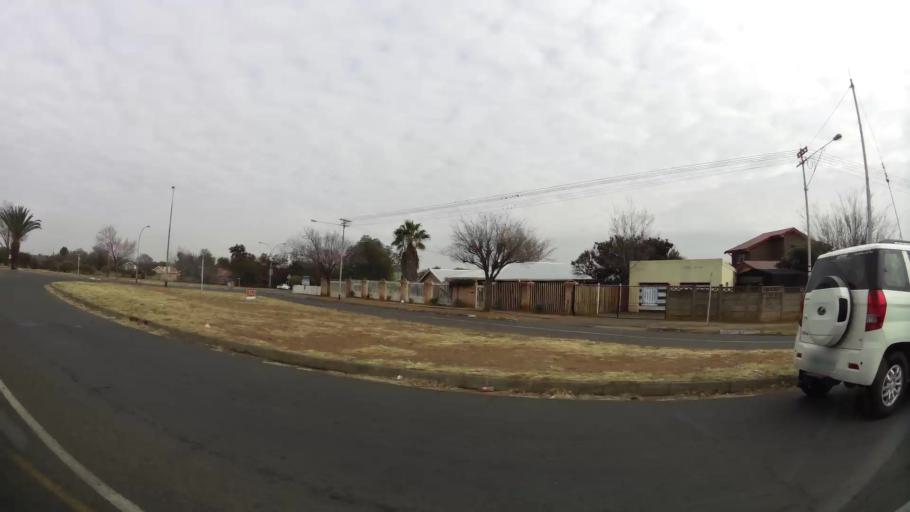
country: ZA
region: Orange Free State
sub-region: Mangaung Metropolitan Municipality
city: Bloemfontein
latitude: -29.1463
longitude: 26.1936
